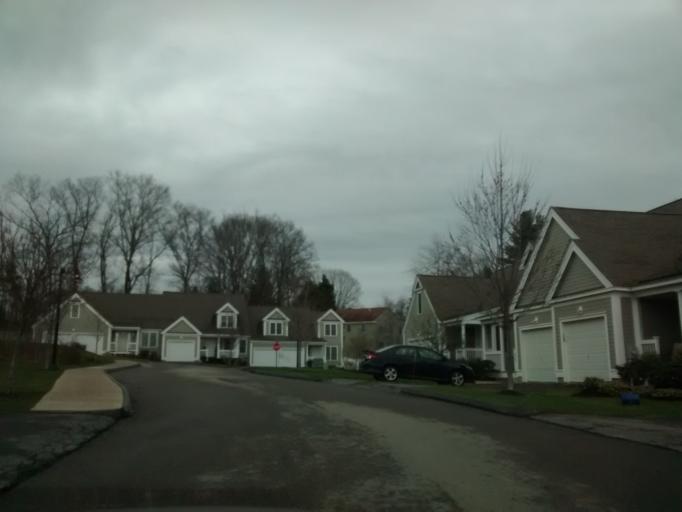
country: US
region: Massachusetts
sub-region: Worcester County
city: Grafton
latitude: 42.2424
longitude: -71.7198
